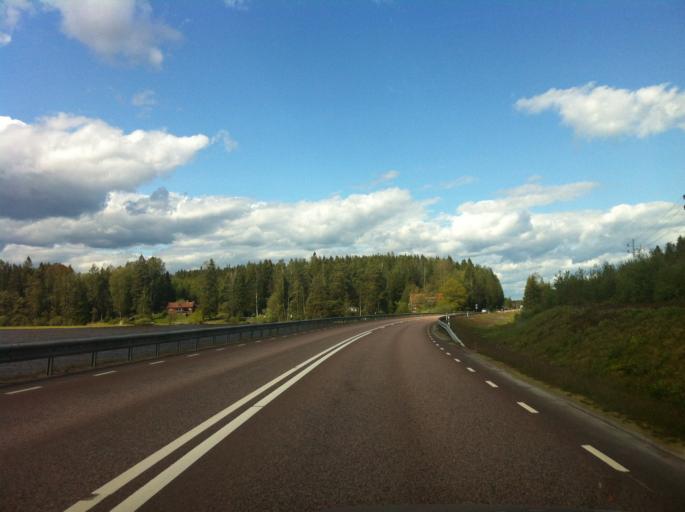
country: SE
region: Vaermland
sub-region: Kristinehamns Kommun
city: Kristinehamn
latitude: 59.3996
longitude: 14.2103
